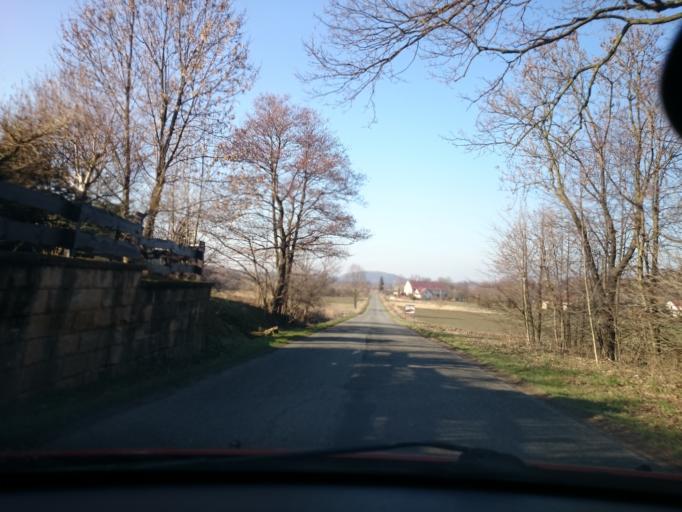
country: PL
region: Lower Silesian Voivodeship
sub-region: Powiat klodzki
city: Bystrzyca Klodzka
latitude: 50.3647
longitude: 16.6376
